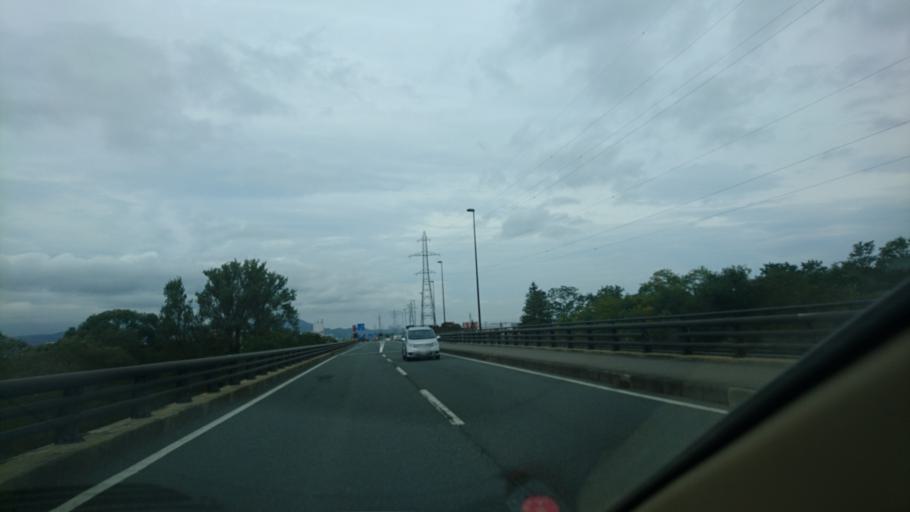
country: JP
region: Iwate
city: Morioka-shi
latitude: 39.7061
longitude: 141.1017
